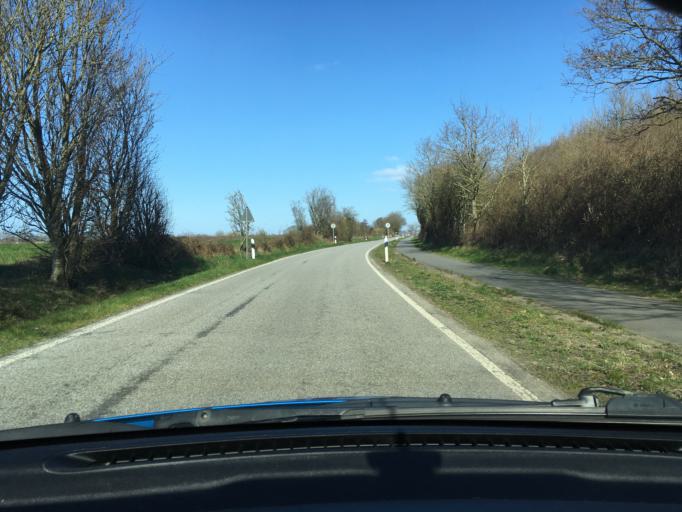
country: DE
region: Schleswig-Holstein
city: Borgwedel
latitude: 54.4959
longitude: 9.6518
